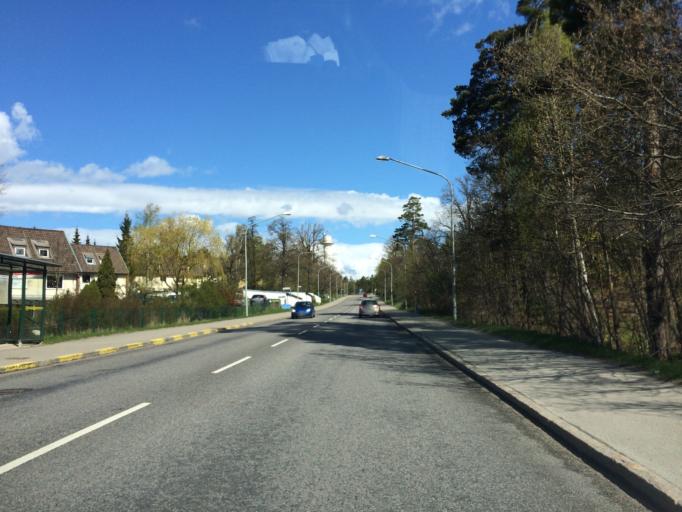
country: SE
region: Stockholm
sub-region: Huddinge Kommun
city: Segeltorp
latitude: 59.2908
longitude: 17.9467
